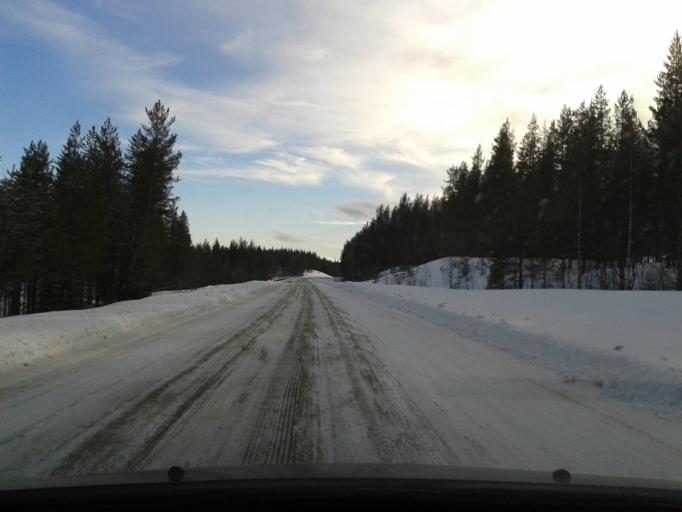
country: SE
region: Vaesterbotten
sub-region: Asele Kommun
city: Asele
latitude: 64.2941
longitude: 17.2586
